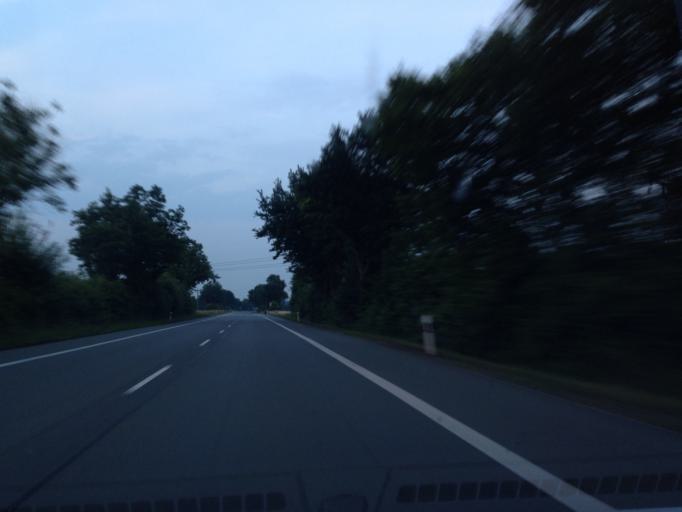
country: DE
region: North Rhine-Westphalia
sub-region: Regierungsbezirk Munster
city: Nordkirchen
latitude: 51.7840
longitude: 7.5123
